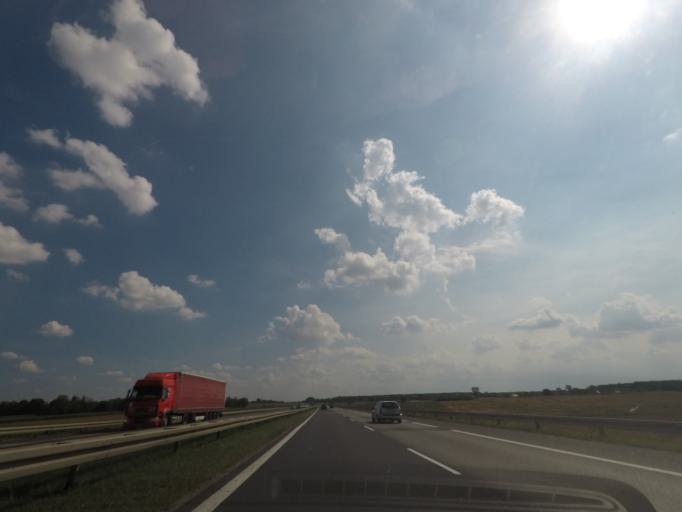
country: PL
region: Lodz Voivodeship
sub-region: Powiat piotrkowski
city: Grabica
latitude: 51.5259
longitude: 19.5995
